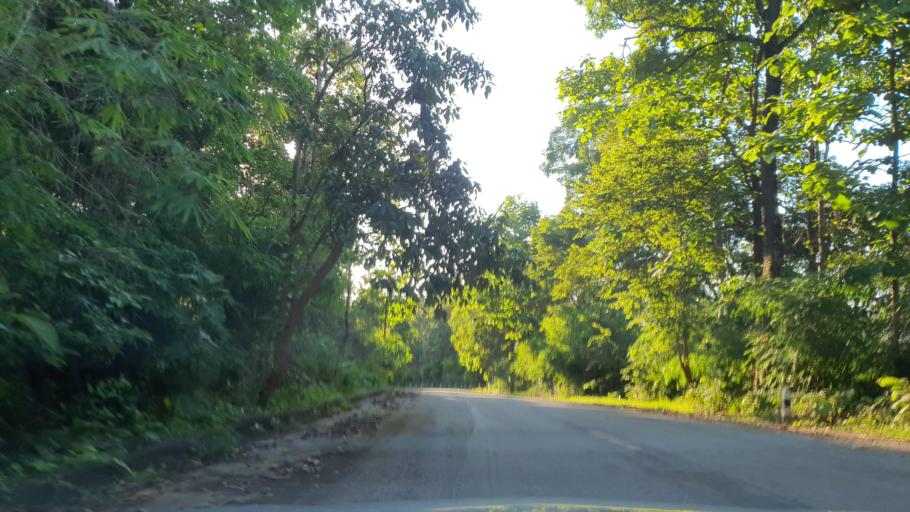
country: TH
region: Chiang Mai
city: Mae On
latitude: 18.8257
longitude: 99.2943
